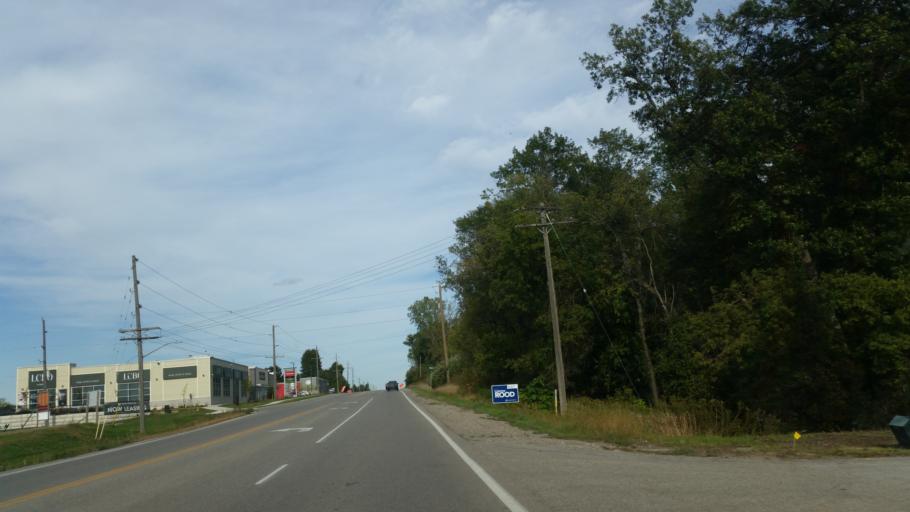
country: CA
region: Ontario
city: Delaware
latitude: 42.9509
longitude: -81.4233
